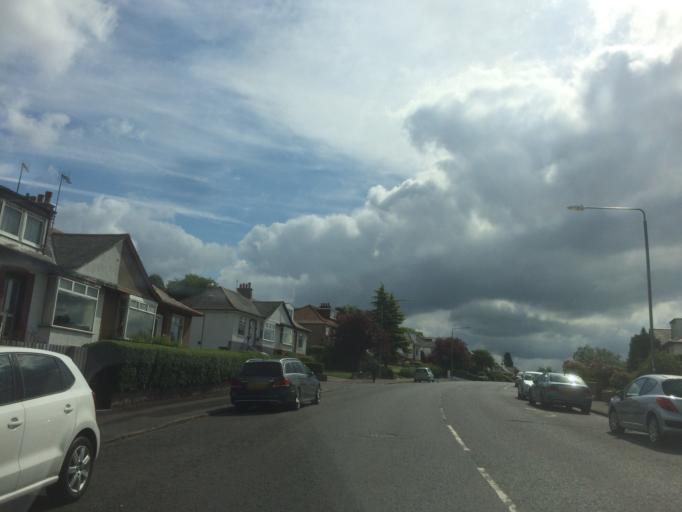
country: GB
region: Scotland
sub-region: East Renfrewshire
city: Giffnock
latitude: 55.8091
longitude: -4.2920
